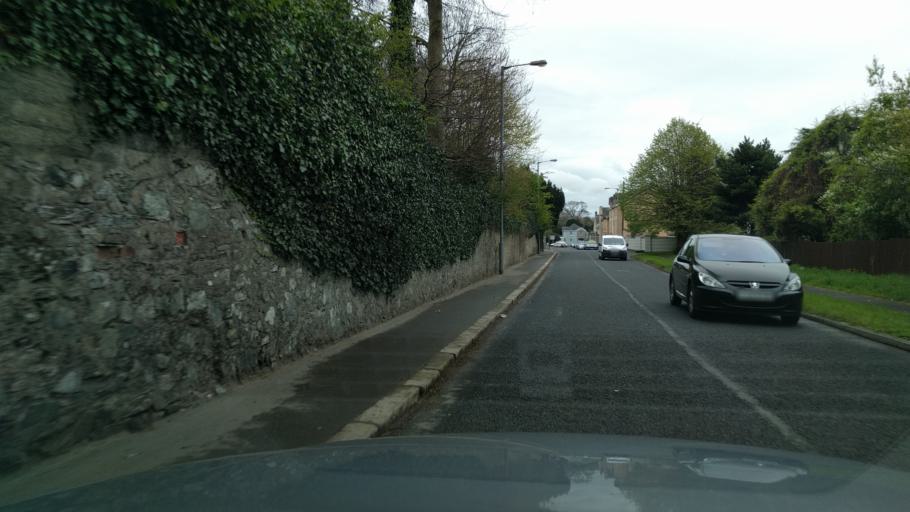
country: GB
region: Northern Ireland
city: Rostrevor
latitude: 54.1027
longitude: -6.2009
